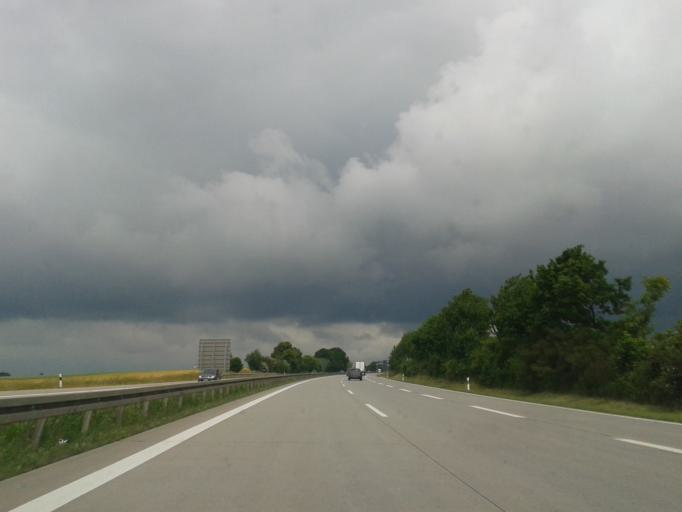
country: DE
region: Saxony
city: Nossen
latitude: 51.0590
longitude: 13.3391
